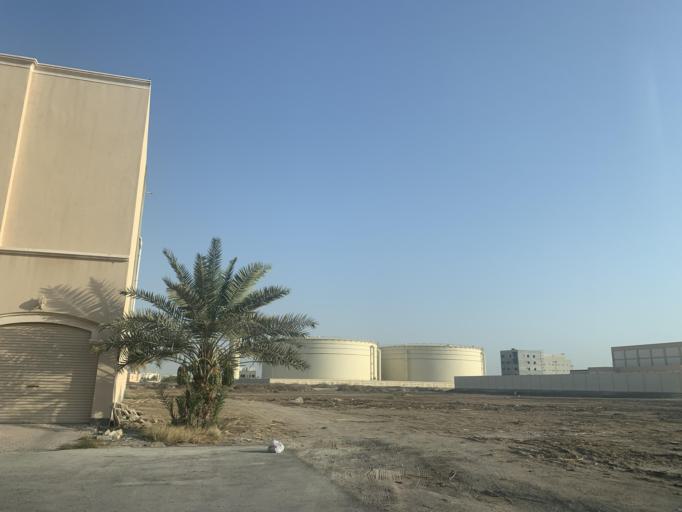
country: BH
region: Manama
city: Jidd Hafs
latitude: 26.2111
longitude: 50.5268
